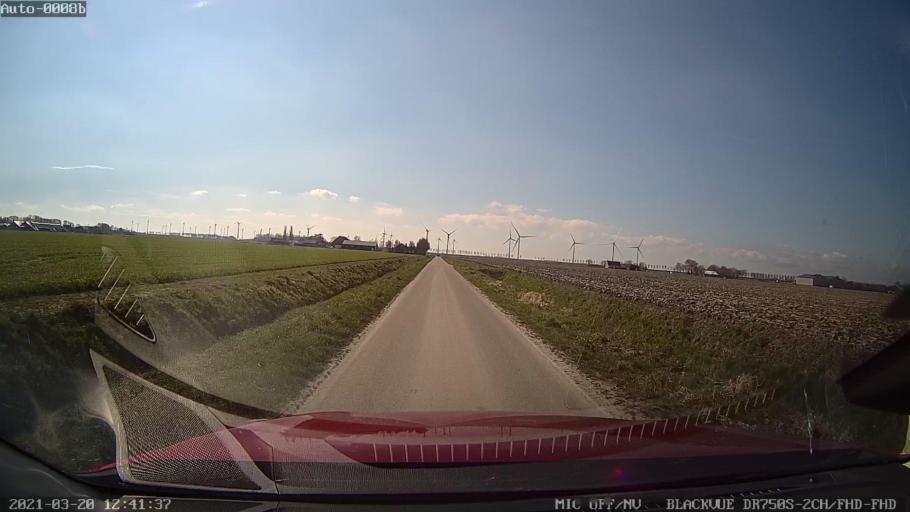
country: NL
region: South Holland
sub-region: Gemeente Goeree-Overflakkee
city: Middelharnis
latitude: 51.7057
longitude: 4.1891
